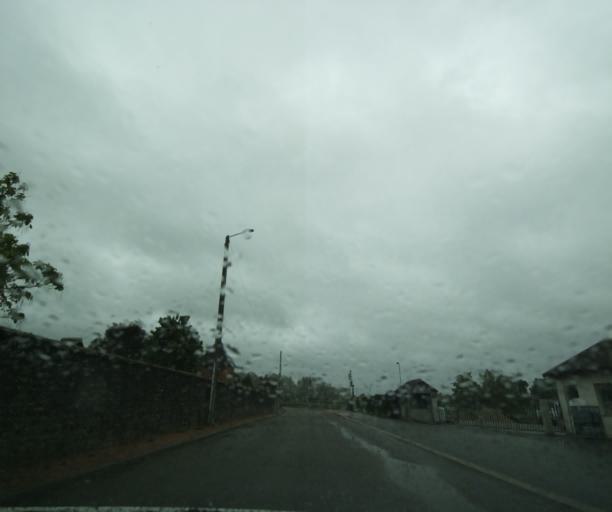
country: FR
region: Bourgogne
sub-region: Departement de Saone-et-Loire
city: Palinges
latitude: 46.5538
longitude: 4.2162
